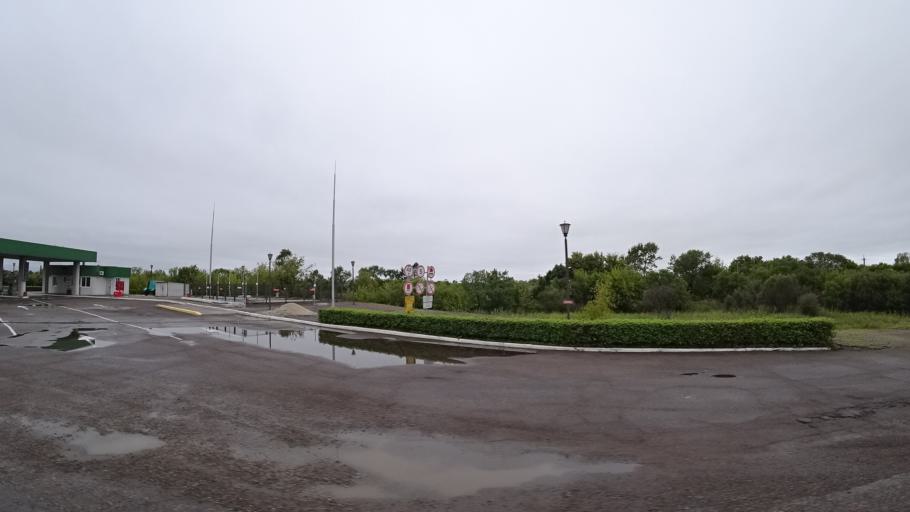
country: RU
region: Primorskiy
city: Monastyrishche
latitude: 44.2155
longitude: 132.4502
